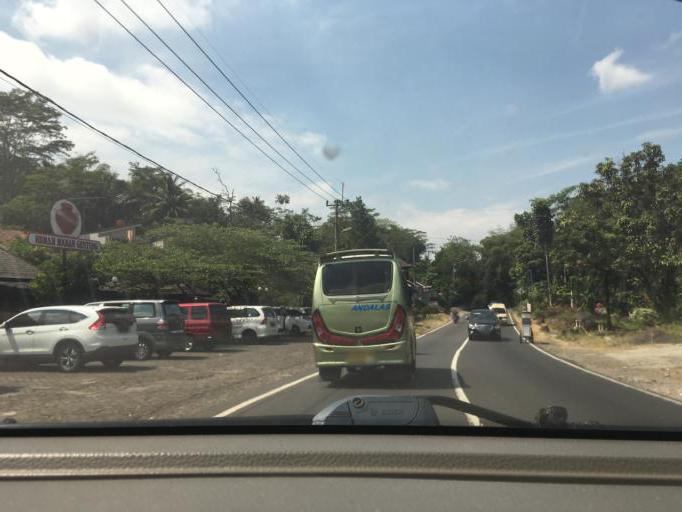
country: ID
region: West Java
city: Tagog
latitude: -7.1171
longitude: 108.1312
